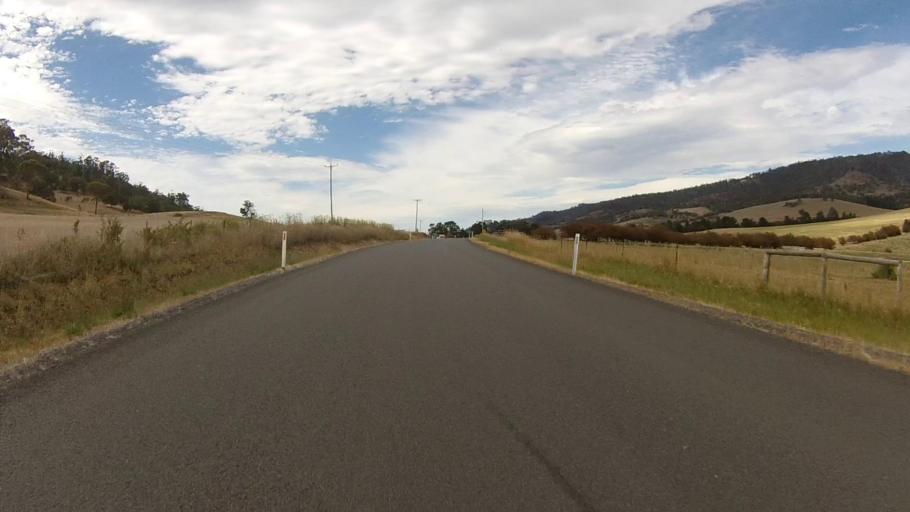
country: AU
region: Tasmania
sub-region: Brighton
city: Old Beach
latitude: -42.7234
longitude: 147.3396
